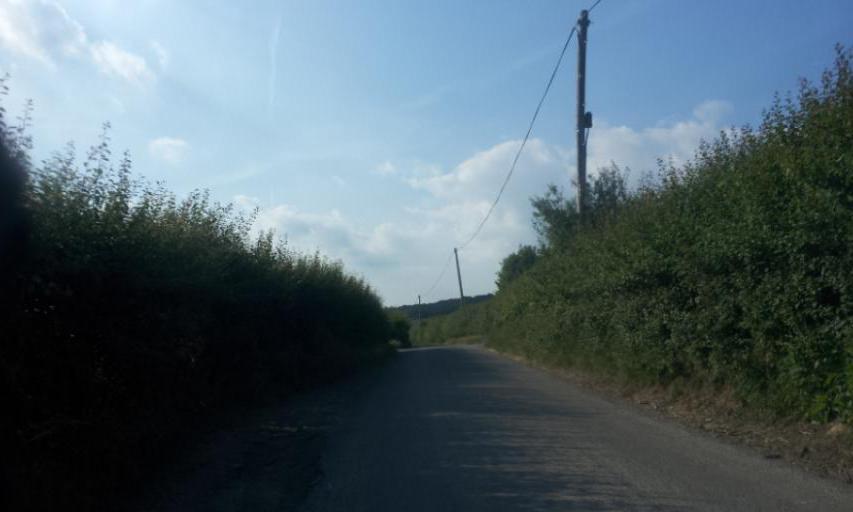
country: GB
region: England
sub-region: Kent
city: Harrietsham
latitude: 51.2741
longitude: 0.6340
